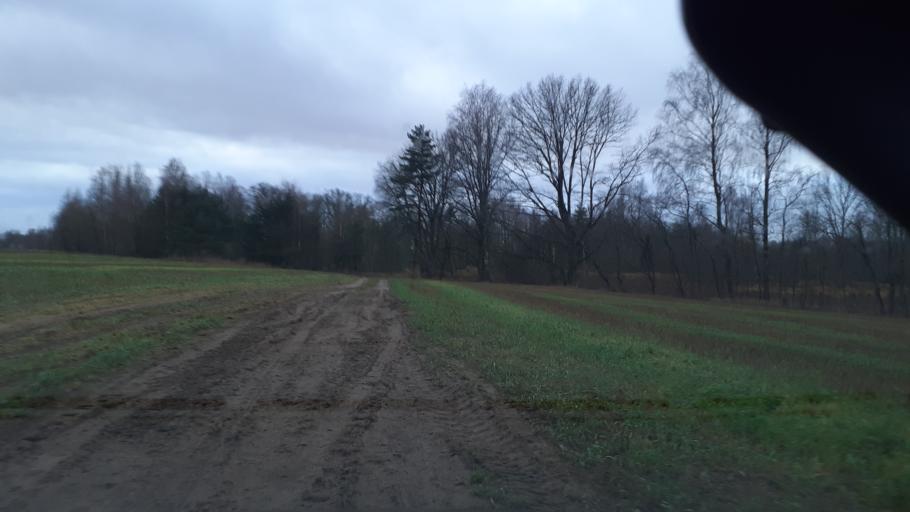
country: LV
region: Kuldigas Rajons
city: Kuldiga
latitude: 56.8809
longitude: 21.7706
